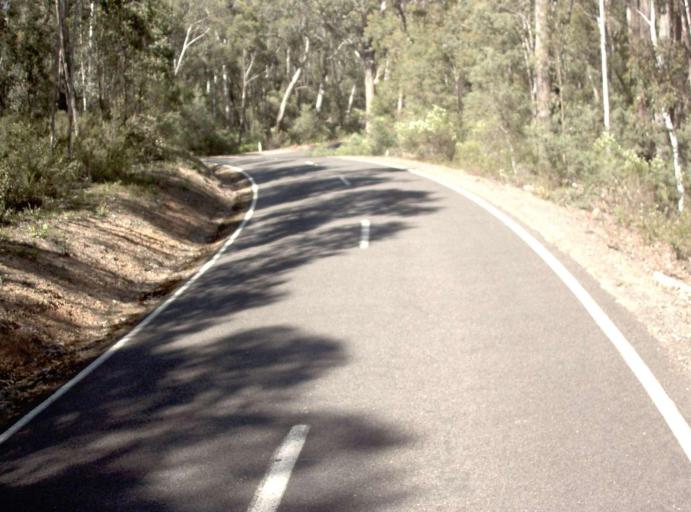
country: AU
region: New South Wales
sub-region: Bombala
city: Bombala
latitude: -37.1382
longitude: 148.7344
